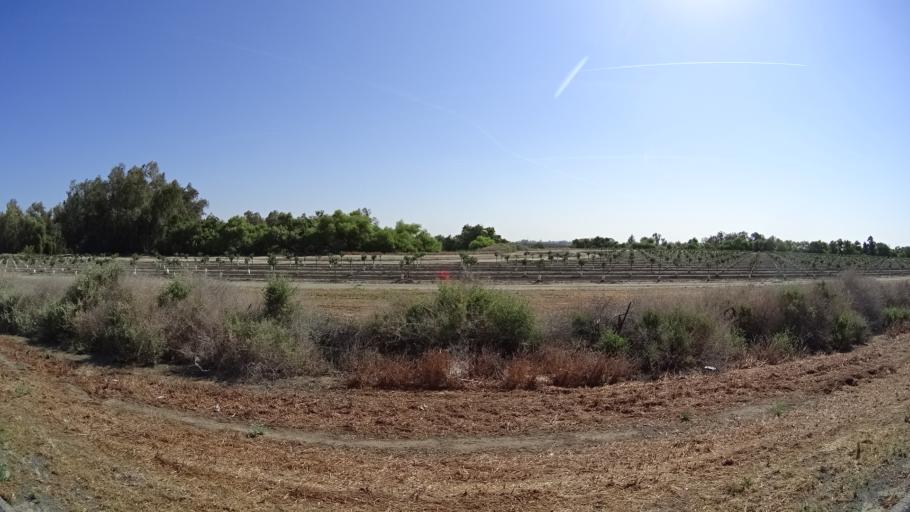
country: US
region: California
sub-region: Fresno County
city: Riverdale
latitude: 36.3647
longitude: -119.9171
